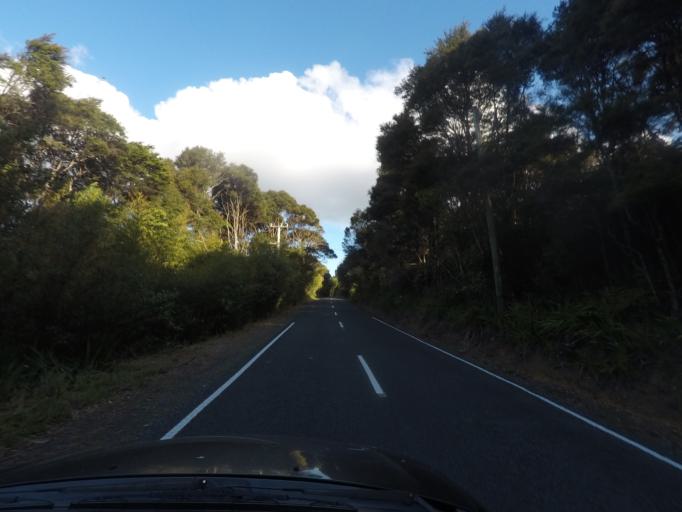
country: NZ
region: Auckland
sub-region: Auckland
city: Titirangi
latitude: -36.9259
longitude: 174.6192
